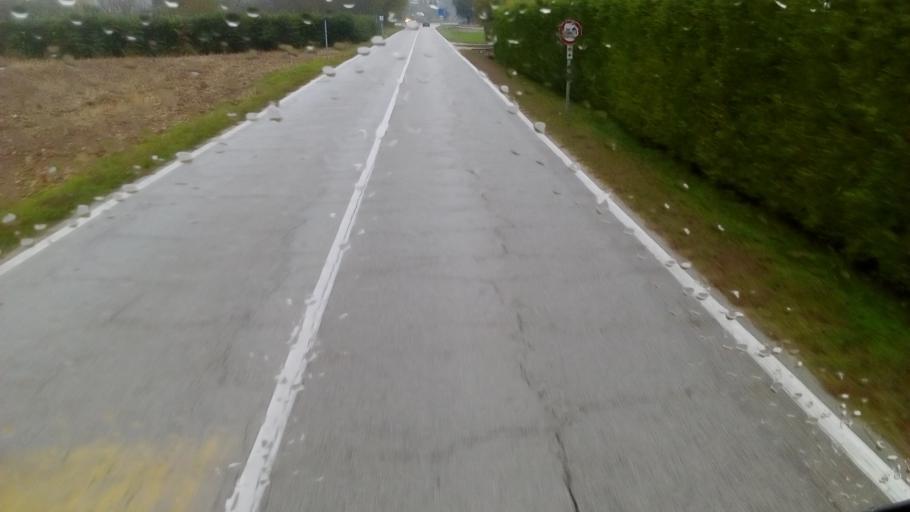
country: IT
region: Veneto
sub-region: Provincia di Vicenza
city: Montecchio Precalcino
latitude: 45.6579
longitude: 11.5702
